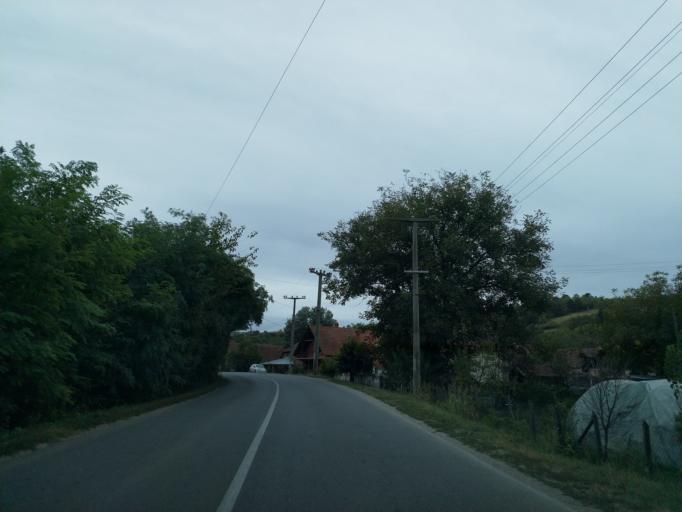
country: RS
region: Central Serbia
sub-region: Pomoravski Okrug
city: Jagodina
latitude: 44.0537
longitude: 21.1806
